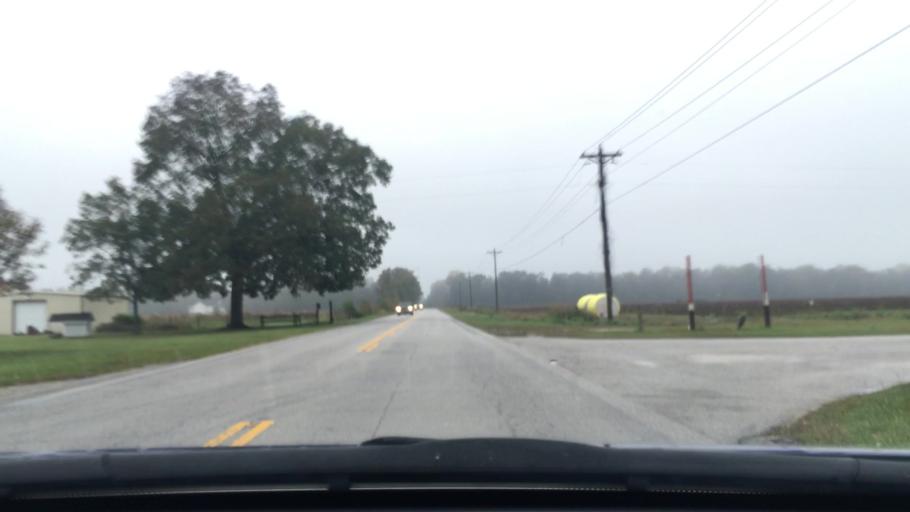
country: US
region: South Carolina
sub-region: Florence County
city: Timmonsville
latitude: 34.2231
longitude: -80.0022
